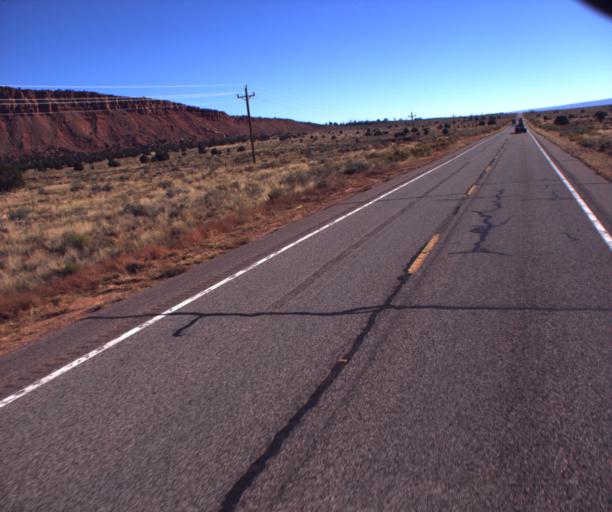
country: US
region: Utah
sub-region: Washington County
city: Hildale
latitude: 36.8579
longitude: -112.7622
